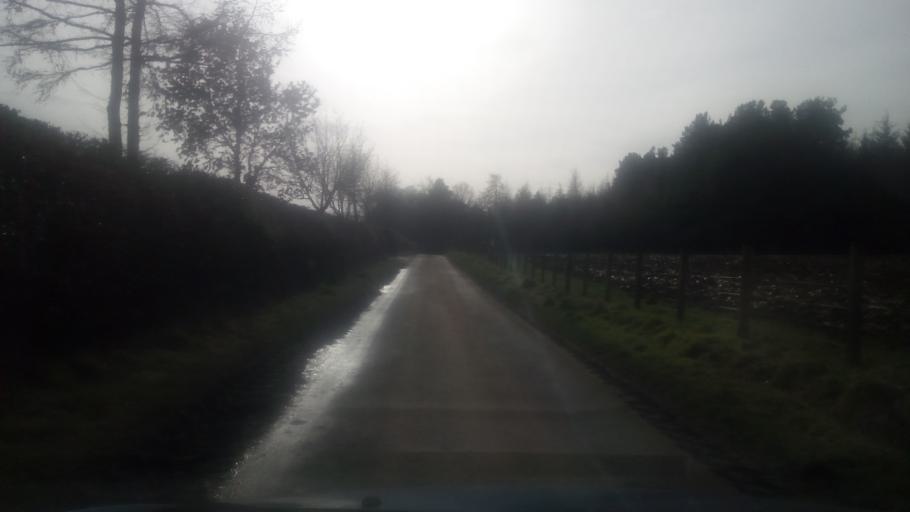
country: GB
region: Scotland
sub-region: The Scottish Borders
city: Jedburgh
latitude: 55.4370
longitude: -2.6404
